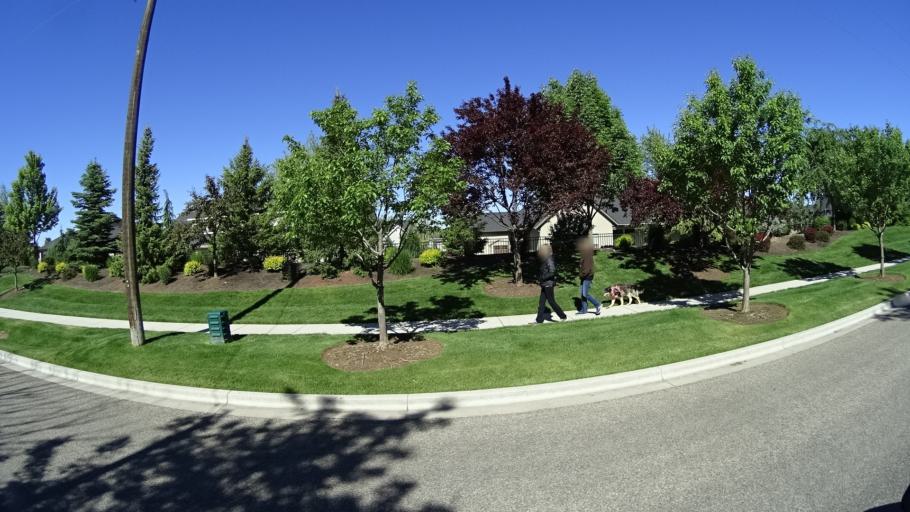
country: US
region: Idaho
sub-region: Ada County
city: Eagle
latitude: 43.6684
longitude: -116.3936
